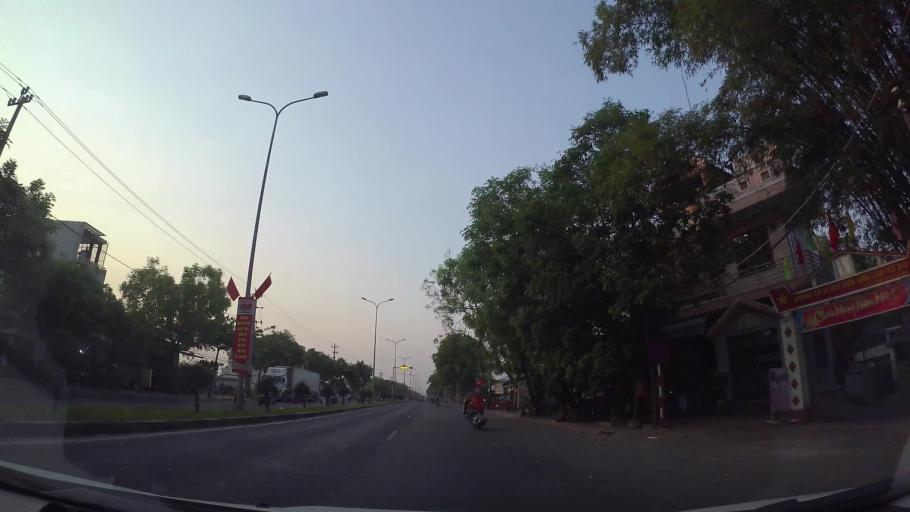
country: VN
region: Da Nang
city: Cam Le
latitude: 15.9514
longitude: 108.2184
